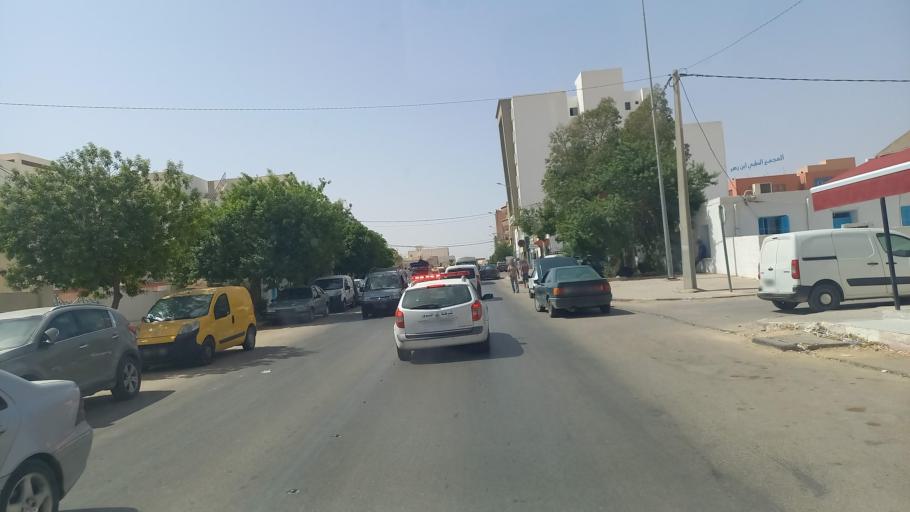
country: TN
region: Madanin
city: Medenine
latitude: 33.3397
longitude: 10.4873
